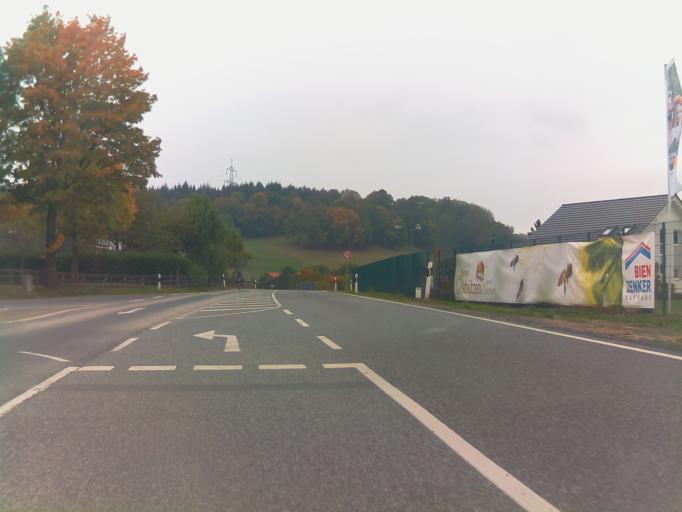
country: DE
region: Hesse
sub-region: Regierungsbezirk Darmstadt
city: Schluchtern
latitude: 50.3846
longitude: 9.5258
